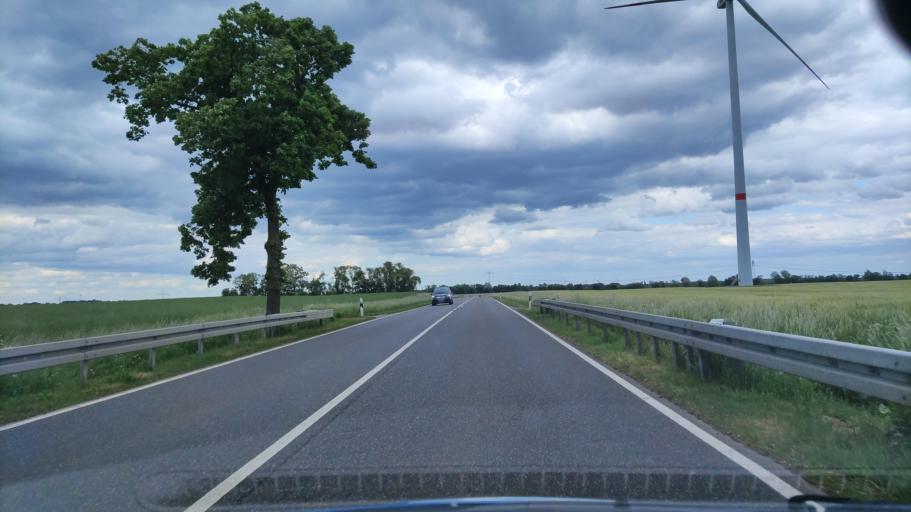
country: DE
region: Mecklenburg-Vorpommern
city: Neuburg
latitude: 53.4430
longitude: 11.9030
